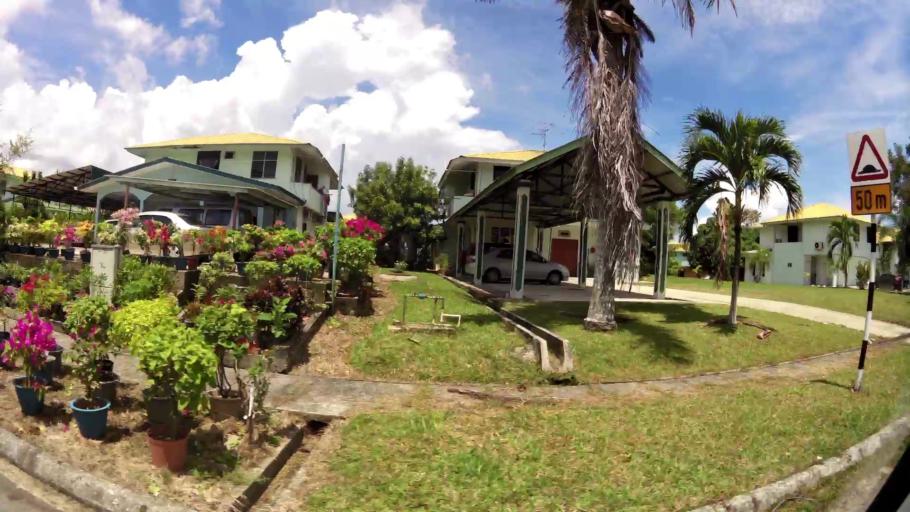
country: BN
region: Brunei and Muara
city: Bandar Seri Begawan
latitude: 4.9608
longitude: 114.9056
